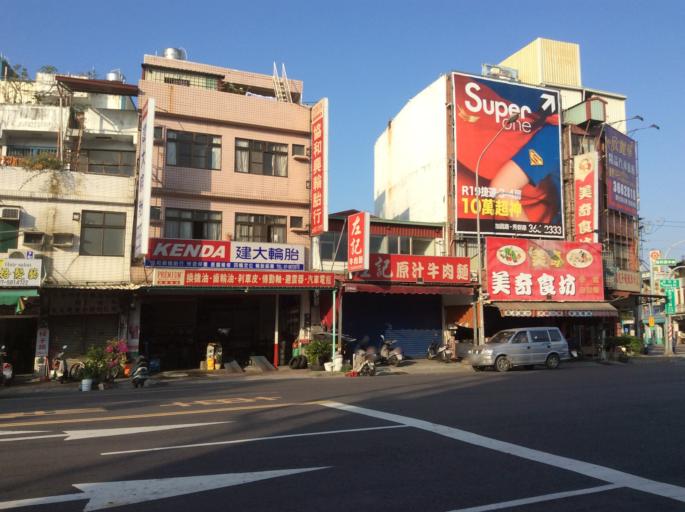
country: TW
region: Kaohsiung
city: Kaohsiung
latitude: 22.6937
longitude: 120.2988
